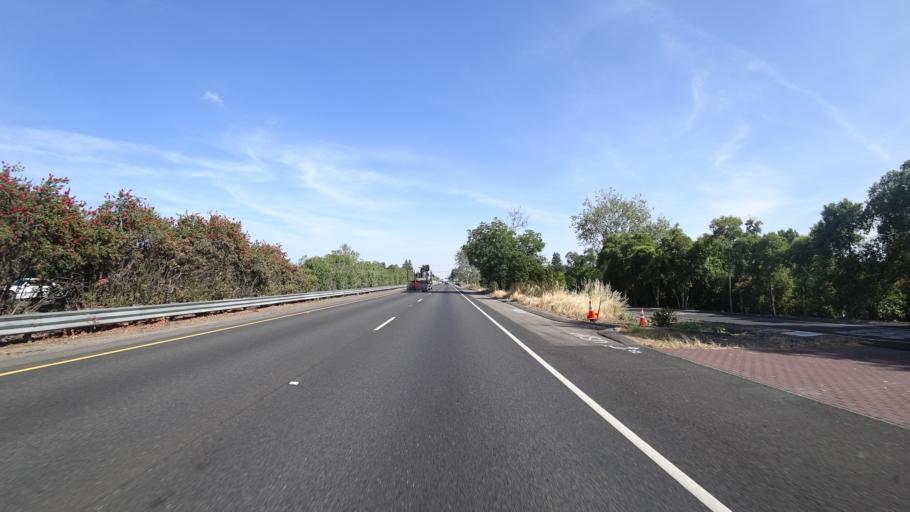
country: US
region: California
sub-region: Butte County
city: Chico
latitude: 39.7463
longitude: -121.8331
